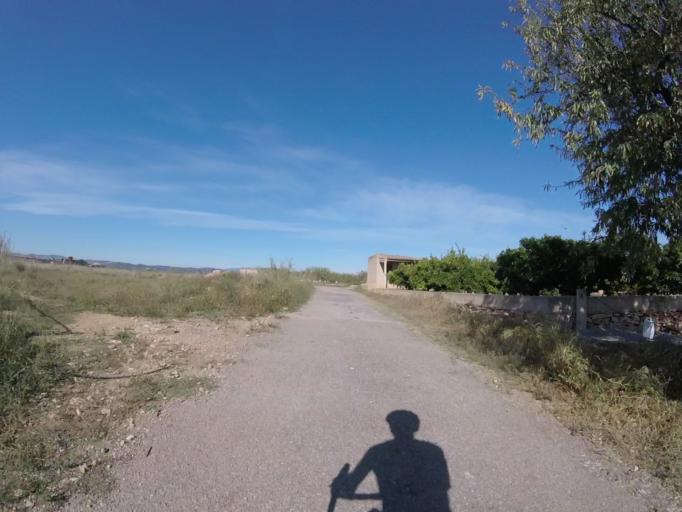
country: ES
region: Valencia
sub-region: Provincia de Castello
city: Torreblanca
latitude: 40.2097
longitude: 0.2332
